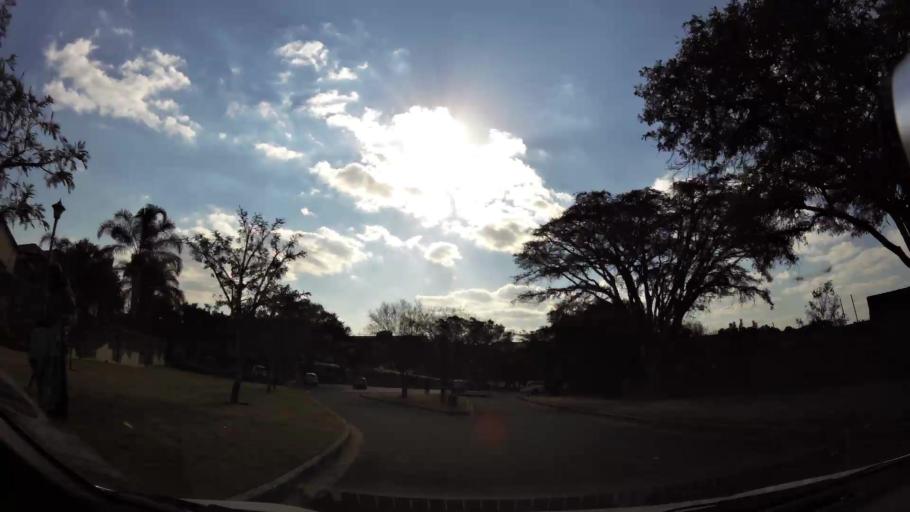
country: ZA
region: Gauteng
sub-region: City of Johannesburg Metropolitan Municipality
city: Diepsloot
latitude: -26.0157
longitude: 28.0271
